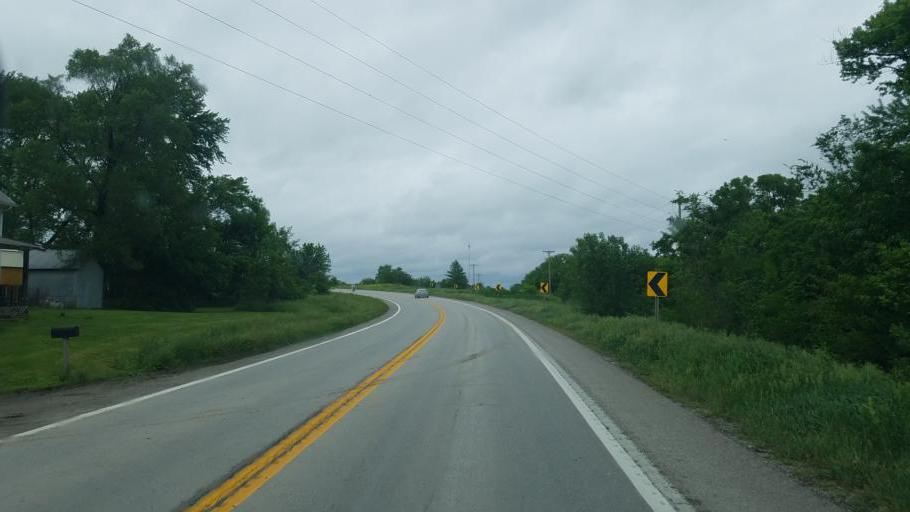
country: US
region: Missouri
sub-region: Livingston County
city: Chillicothe
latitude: 39.6603
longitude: -93.4792
